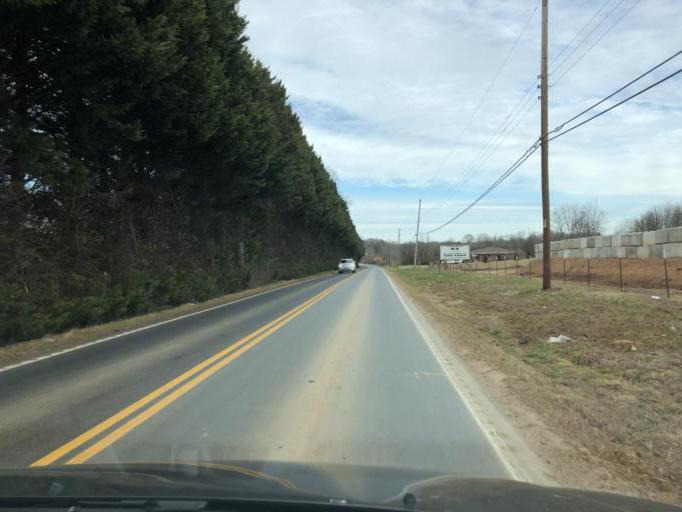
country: US
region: South Carolina
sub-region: Greenville County
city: Five Forks
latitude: 34.8647
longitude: -82.1990
